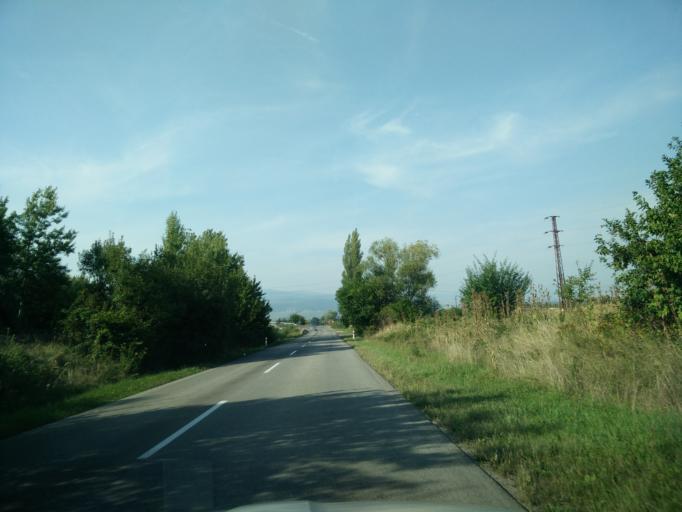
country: SK
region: Nitriansky
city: Novaky
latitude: 48.7213
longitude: 18.5760
